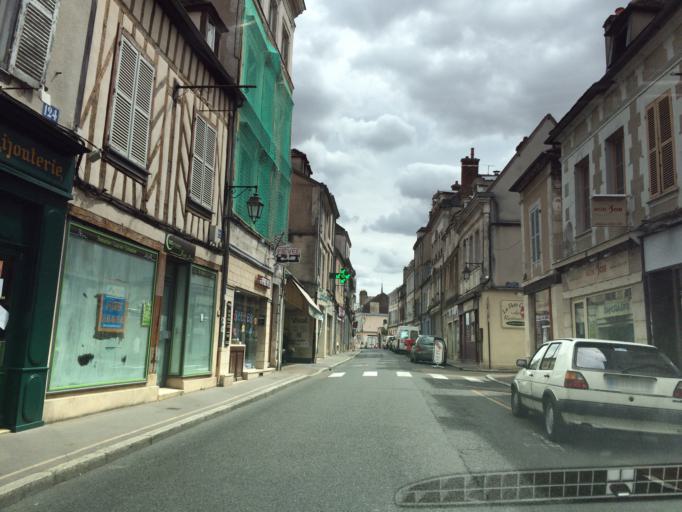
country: FR
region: Bourgogne
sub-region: Departement de l'Yonne
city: Auxerre
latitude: 47.7996
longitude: 3.5686
